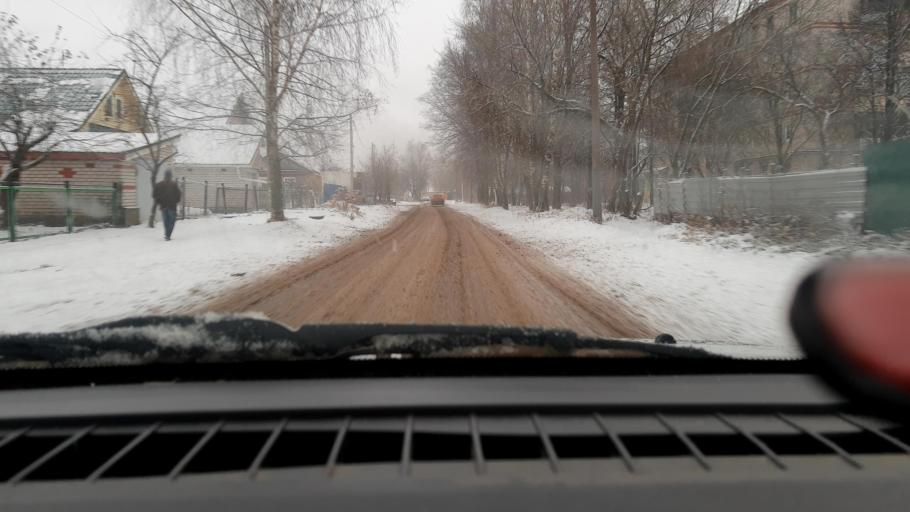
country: RU
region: Nizjnij Novgorod
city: Kstovo
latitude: 56.1411
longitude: 44.1996
